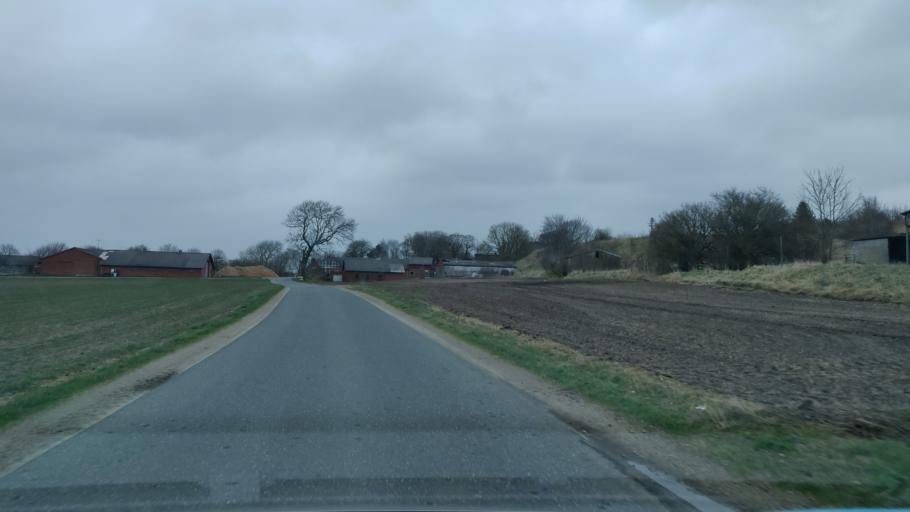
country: DK
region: Central Jutland
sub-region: Skive Kommune
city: Hojslev
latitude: 56.5517
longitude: 9.2448
